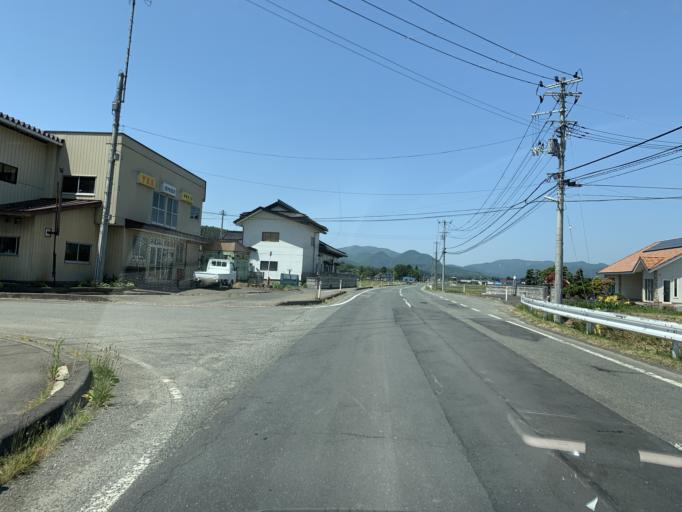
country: JP
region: Iwate
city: Kitakami
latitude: 39.2830
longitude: 141.0384
